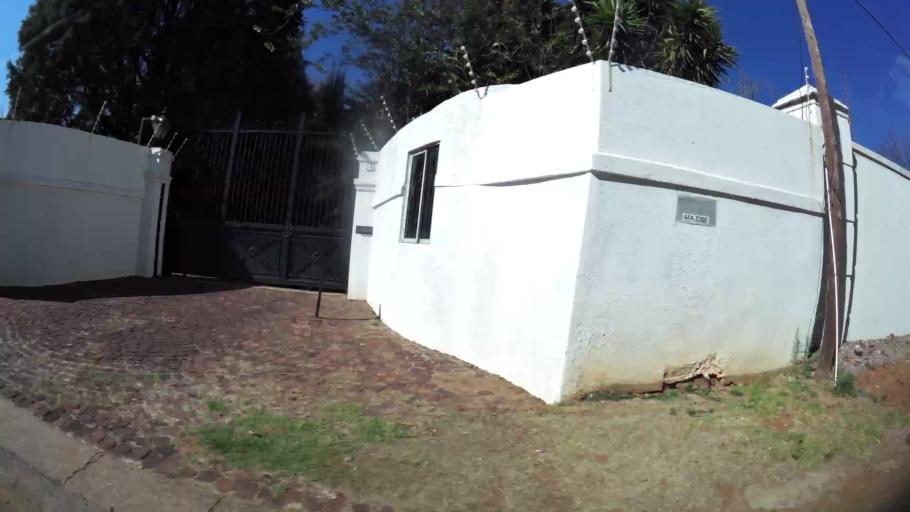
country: ZA
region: Gauteng
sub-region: City of Johannesburg Metropolitan Municipality
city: Johannesburg
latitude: -26.1312
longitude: 28.0398
